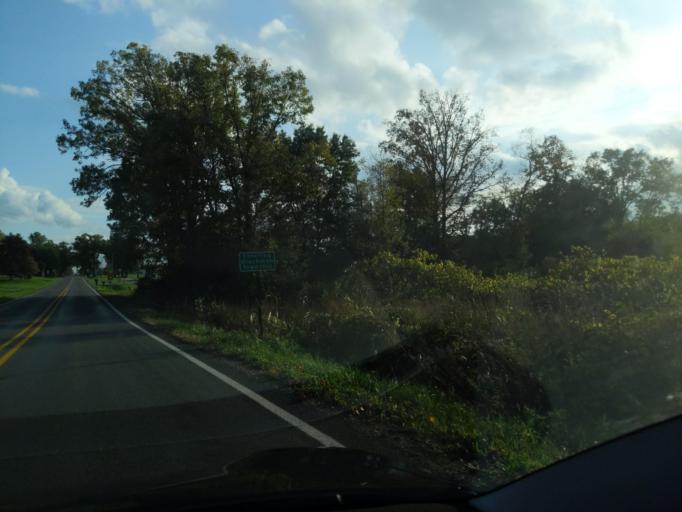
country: US
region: Michigan
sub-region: Jackson County
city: Jackson
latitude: 42.3348
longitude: -84.4629
